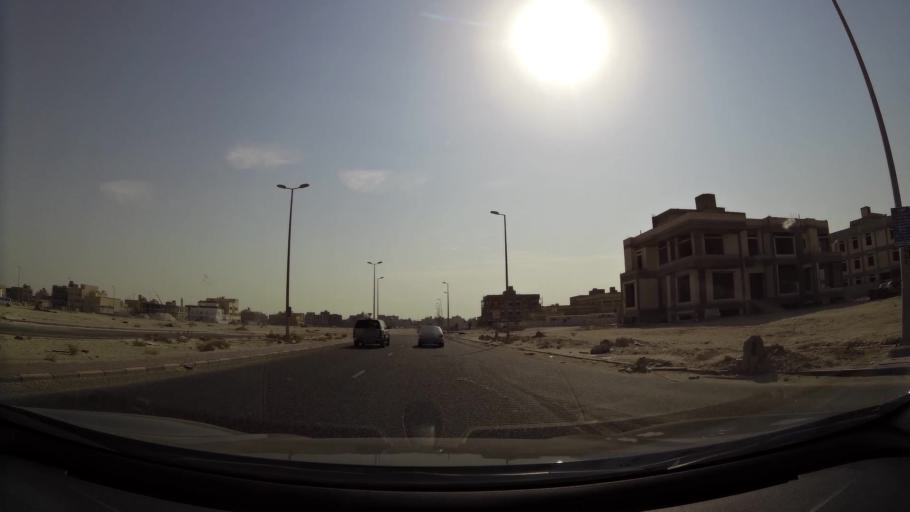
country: KW
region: Al Ahmadi
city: Al Wafrah
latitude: 28.7878
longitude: 48.0446
